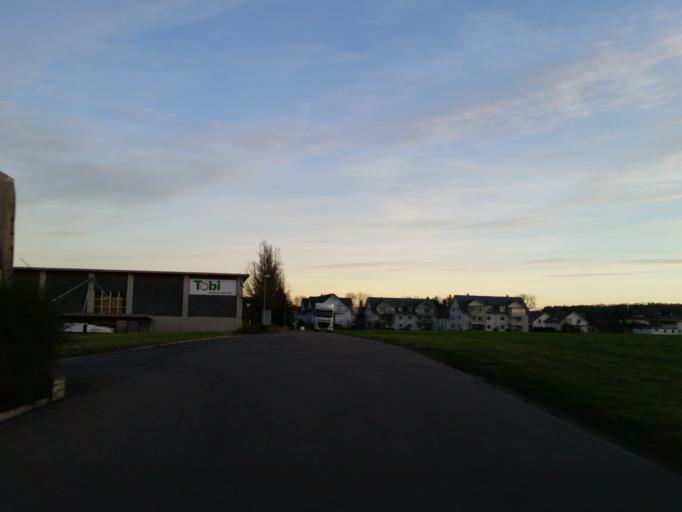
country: CH
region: Thurgau
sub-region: Kreuzlingen District
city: Guttingen
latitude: 47.6093
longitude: 9.2897
